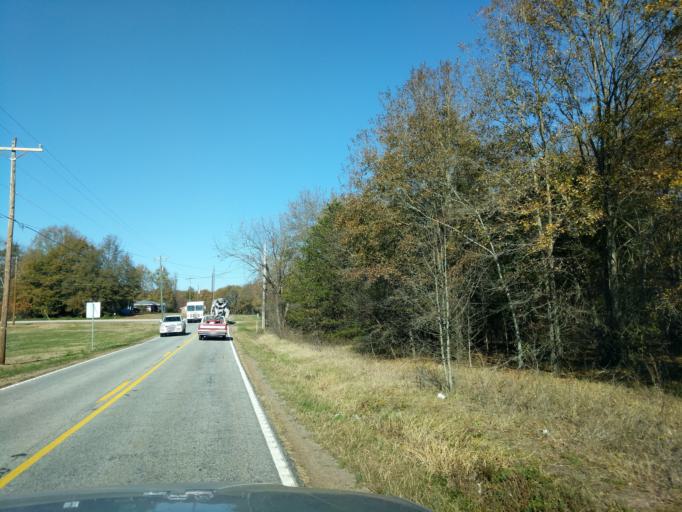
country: US
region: South Carolina
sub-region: Spartanburg County
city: Duncan
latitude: 34.9962
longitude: -82.1774
